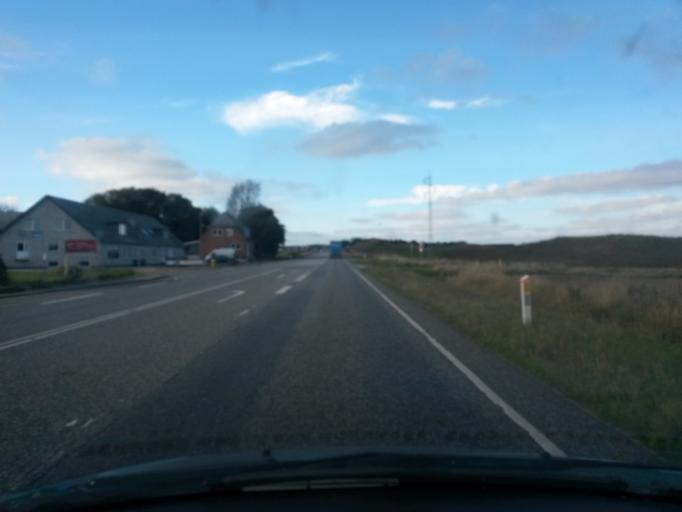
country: DK
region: Central Jutland
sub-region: Holstebro Kommune
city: Holstebro
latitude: 56.3292
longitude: 8.6598
